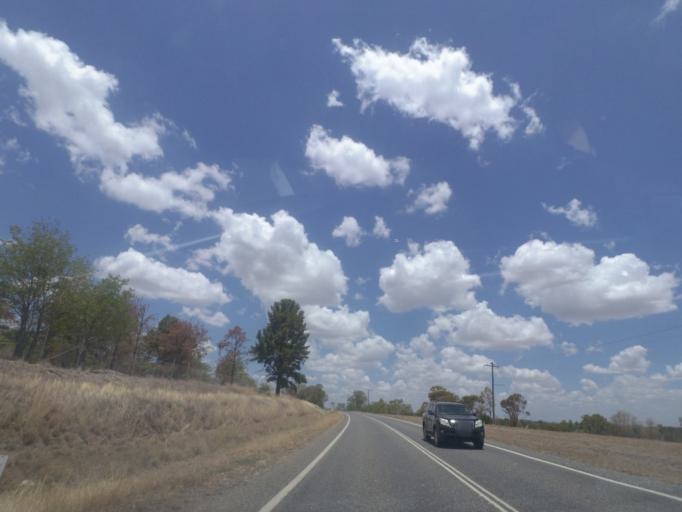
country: AU
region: Queensland
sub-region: Southern Downs
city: Warwick
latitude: -28.0269
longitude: 151.9853
